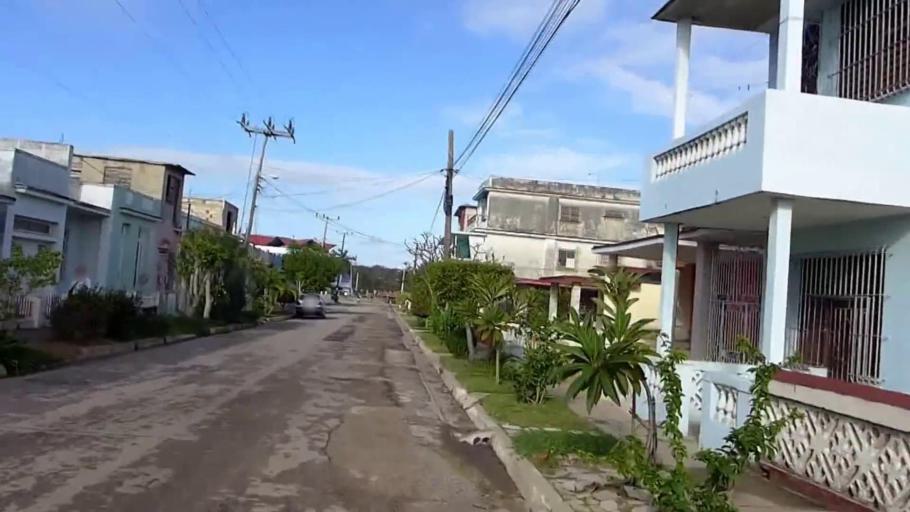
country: CU
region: Camaguey
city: Camaguey
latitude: 21.3835
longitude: -77.9293
